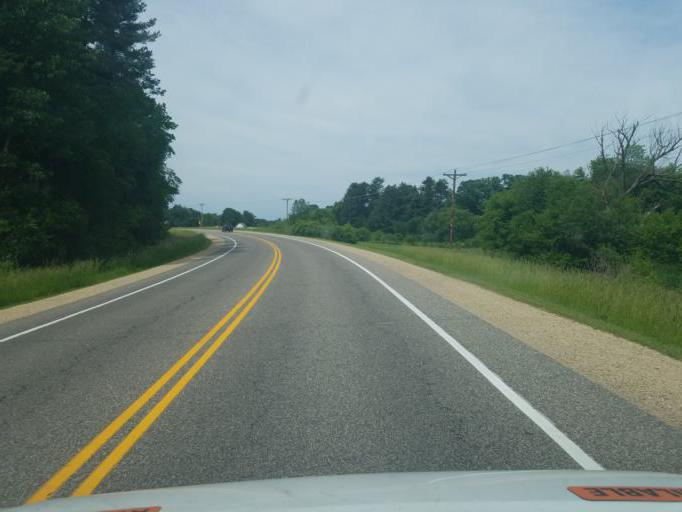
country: US
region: Wisconsin
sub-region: Juneau County
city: Elroy
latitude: 43.7672
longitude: -90.2347
